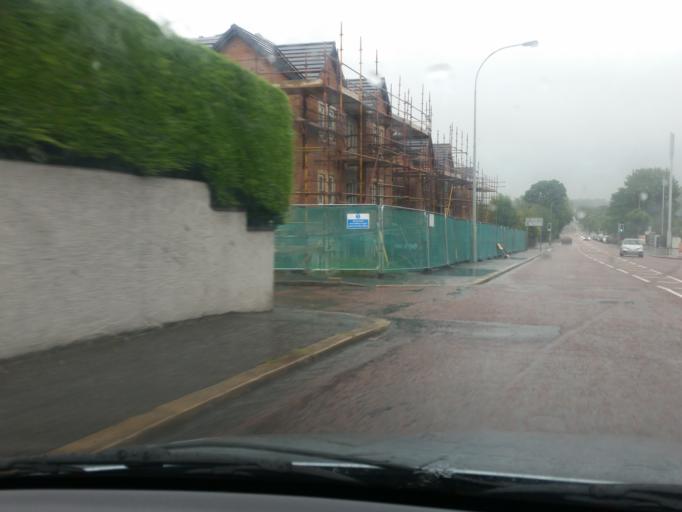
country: GB
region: Northern Ireland
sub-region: Castlereagh District
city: Castlereagh
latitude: 54.6057
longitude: -5.8719
